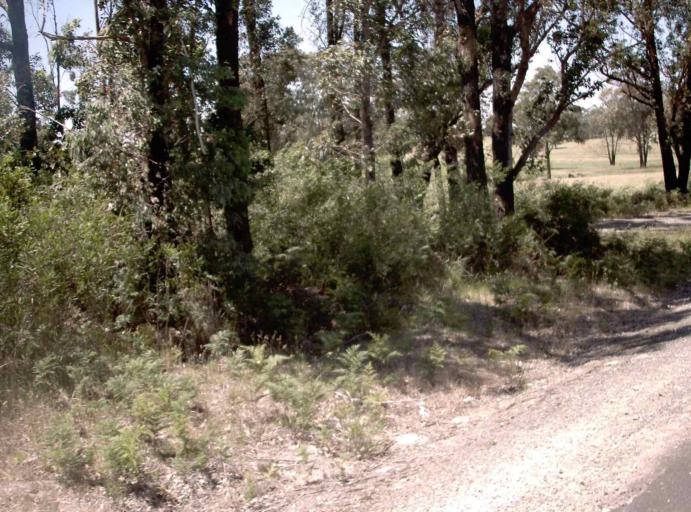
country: AU
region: Victoria
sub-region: East Gippsland
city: Lakes Entrance
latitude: -37.7523
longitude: 148.2945
